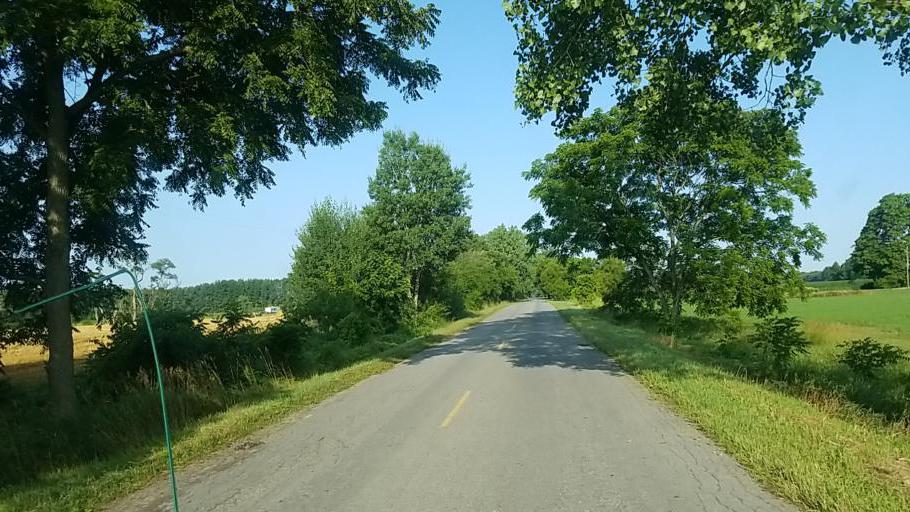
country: US
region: Michigan
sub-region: Newaygo County
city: Fremont
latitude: 43.4821
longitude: -86.0632
